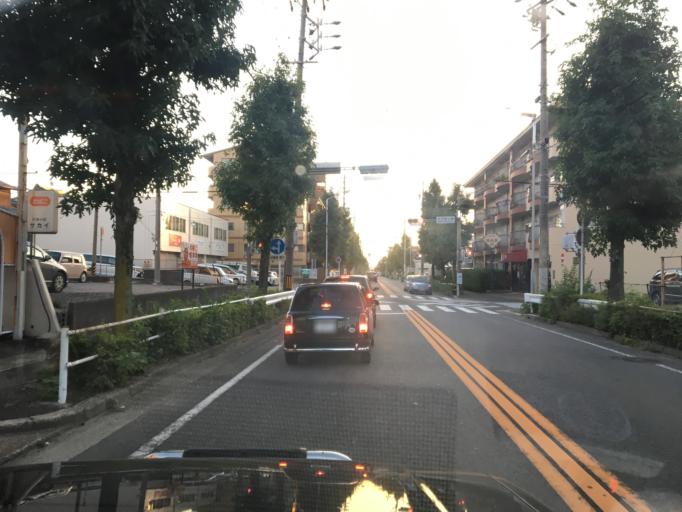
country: JP
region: Aichi
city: Kasugai
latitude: 35.1984
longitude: 137.0072
